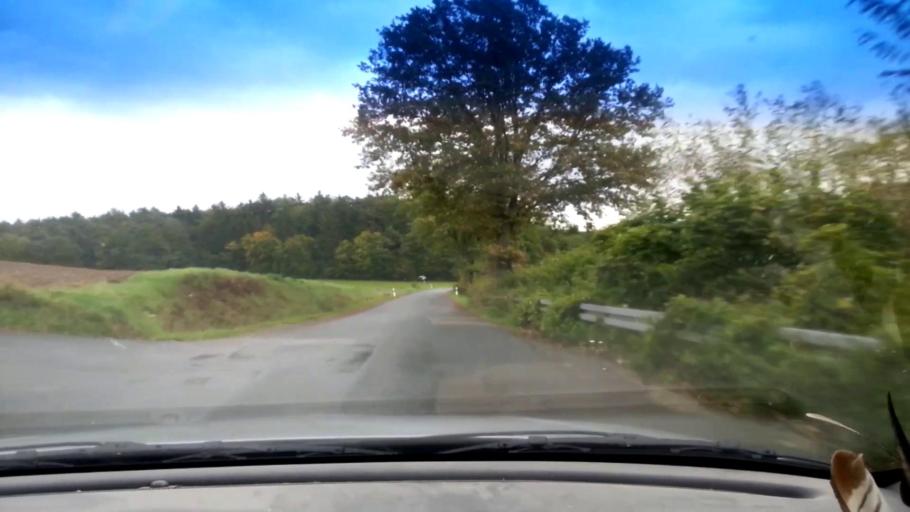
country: DE
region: Bavaria
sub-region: Upper Franconia
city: Burgebrach
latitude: 49.8072
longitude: 10.7039
